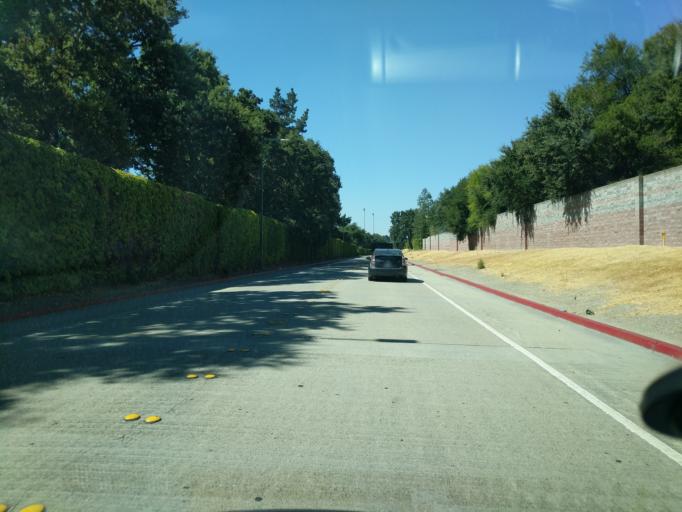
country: US
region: California
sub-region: Contra Costa County
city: Walnut Creek
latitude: 37.8869
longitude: -122.0515
